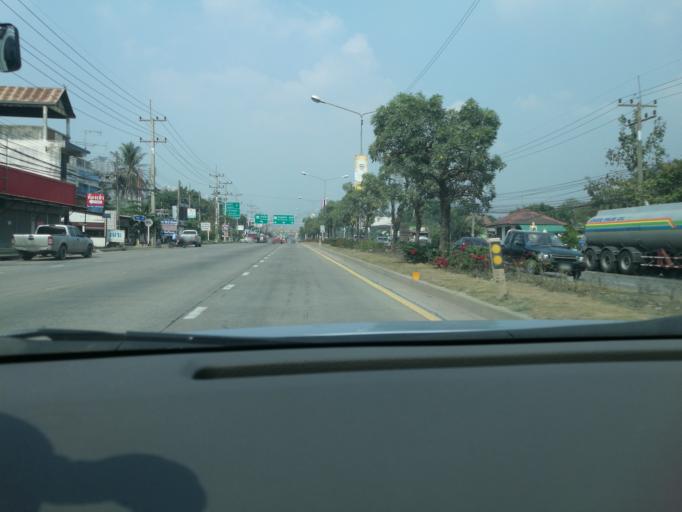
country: TH
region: Sara Buri
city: Chaloem Phra Kiat
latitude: 14.6853
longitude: 100.8725
